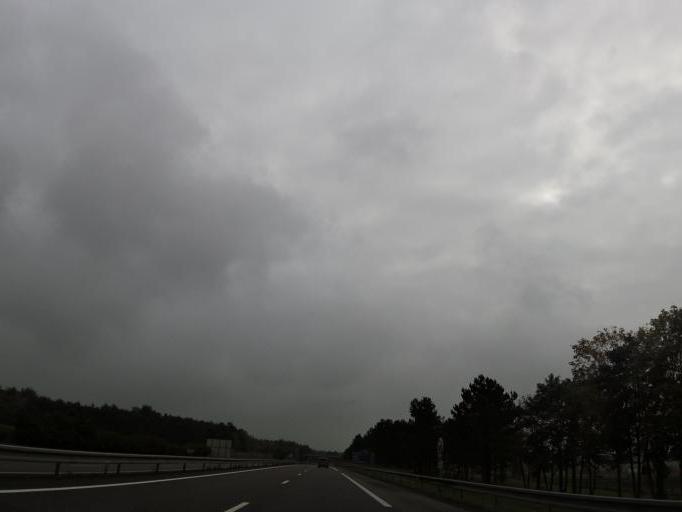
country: FR
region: Champagne-Ardenne
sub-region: Departement de la Marne
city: Fagnieres
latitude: 49.0405
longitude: 4.3352
